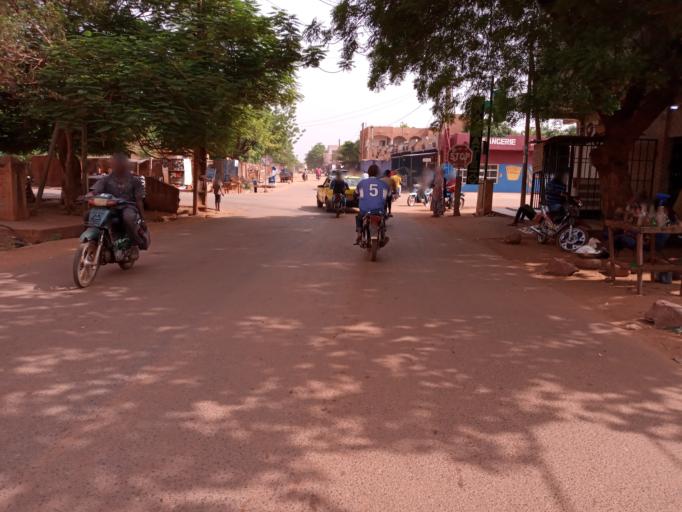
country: ML
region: Bamako
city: Bamako
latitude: 12.6101
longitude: -7.9528
